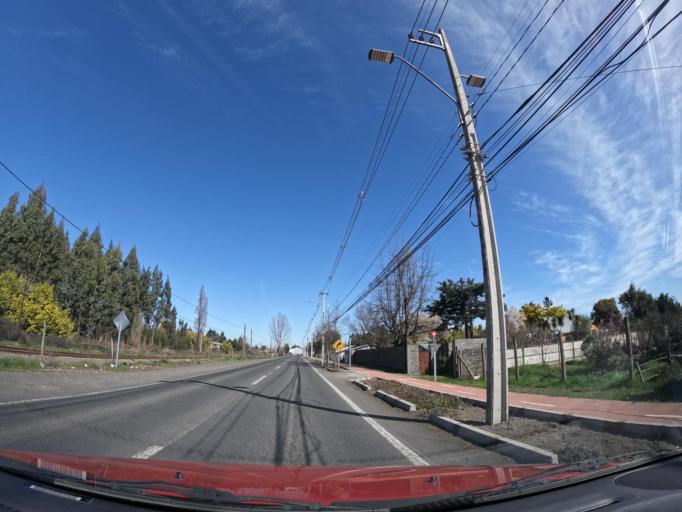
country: CL
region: Biobio
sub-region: Provincia de Biobio
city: Cabrero
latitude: -37.0778
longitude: -72.4341
